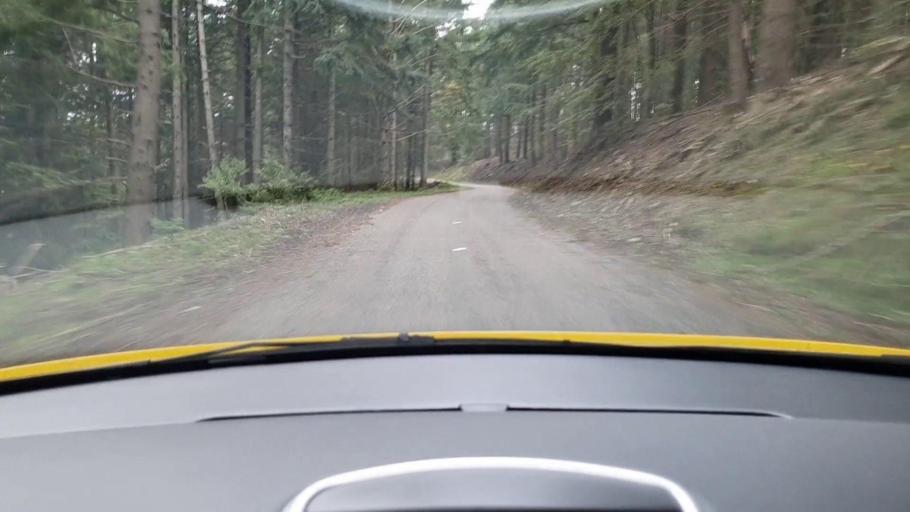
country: FR
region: Languedoc-Roussillon
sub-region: Departement de la Lozere
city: Meyrueis
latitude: 44.0913
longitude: 3.4566
